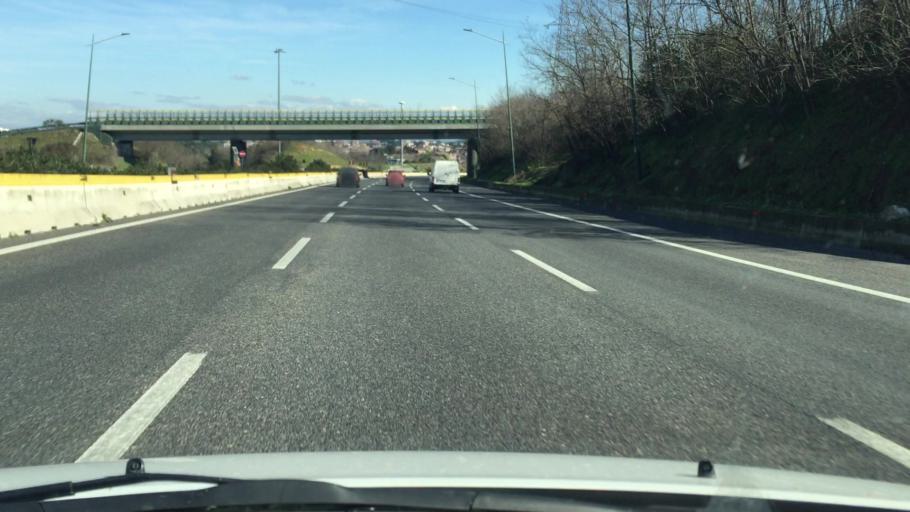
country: VA
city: Vatican City
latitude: 41.9837
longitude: 12.4652
